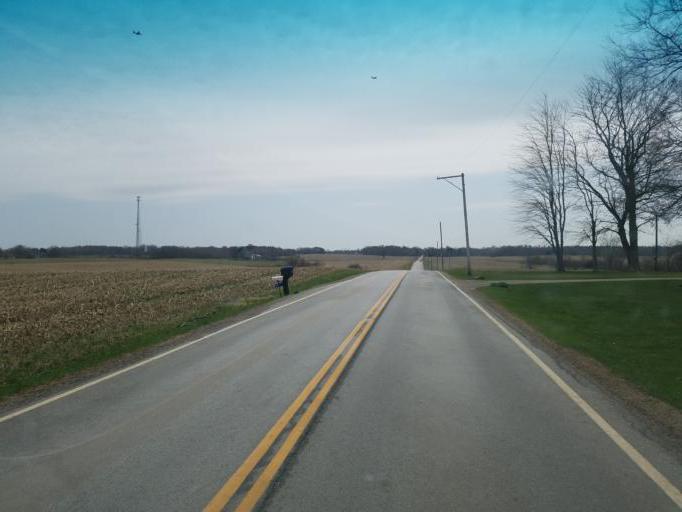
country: US
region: Ohio
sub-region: Crawford County
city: Galion
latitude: 40.7170
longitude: -82.7318
